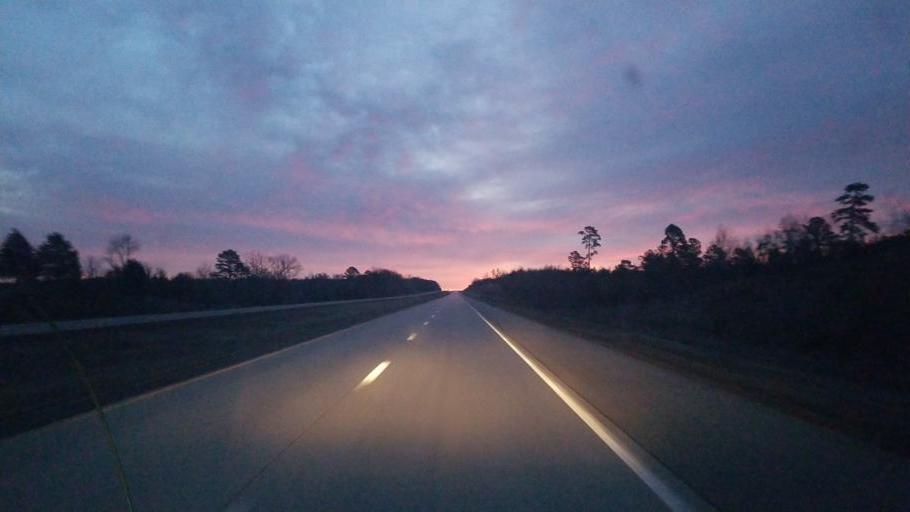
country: US
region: Missouri
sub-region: Shannon County
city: Winona
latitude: 36.9989
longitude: -91.4205
